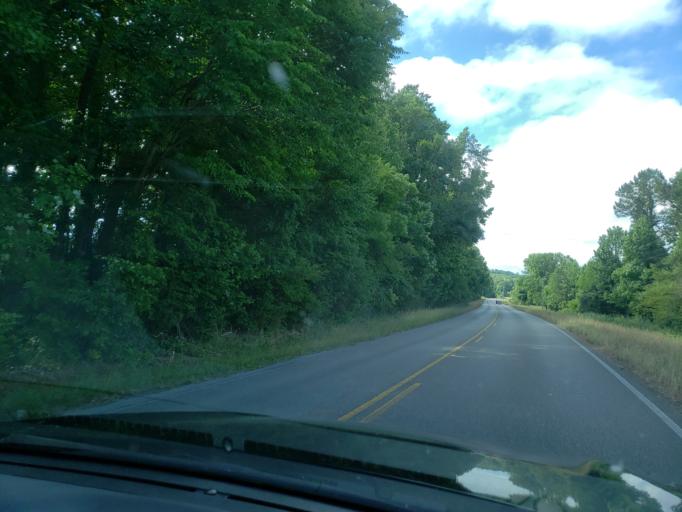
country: US
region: Alabama
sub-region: Calhoun County
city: Weaver
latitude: 33.7455
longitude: -85.8471
